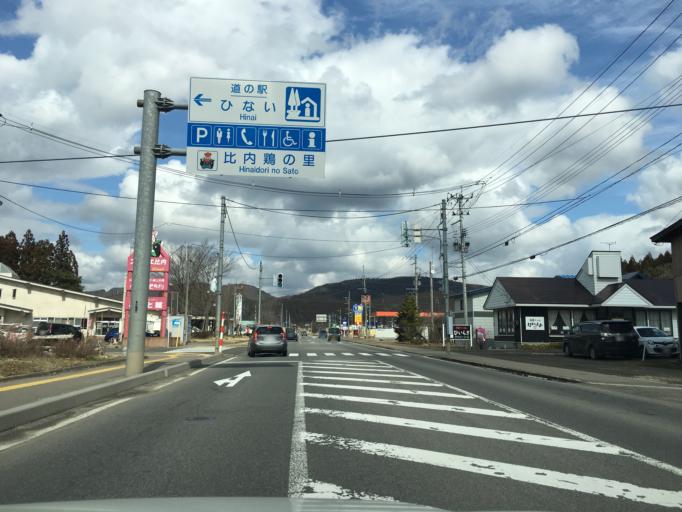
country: JP
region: Akita
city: Odate
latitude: 40.2187
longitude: 140.5856
